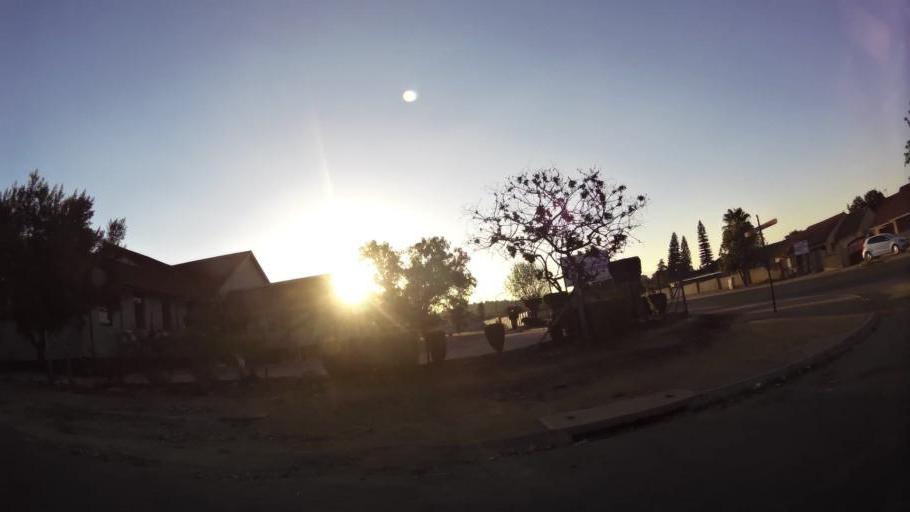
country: ZA
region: North-West
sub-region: Bojanala Platinum District Municipality
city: Rustenburg
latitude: -25.6392
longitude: 27.2035
